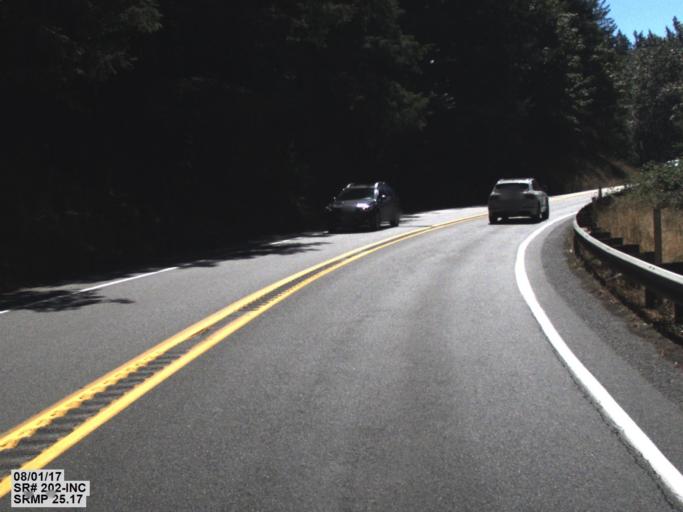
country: US
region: Washington
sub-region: King County
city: Snoqualmie
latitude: 47.5497
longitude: -121.8385
